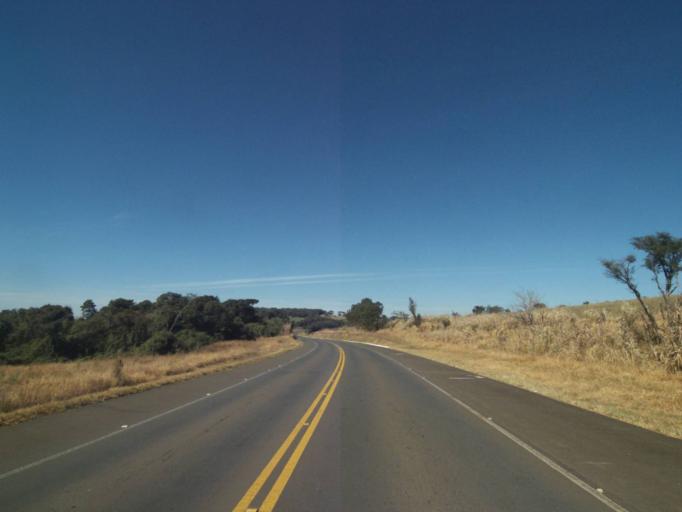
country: BR
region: Parana
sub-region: Tibagi
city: Tibagi
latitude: -24.7706
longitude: -50.4666
